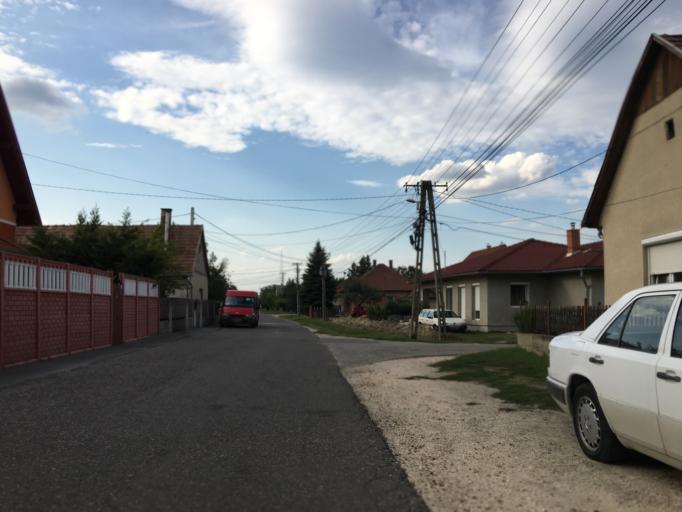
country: HU
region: Pest
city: Szigetszentmiklos
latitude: 47.3546
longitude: 19.0296
